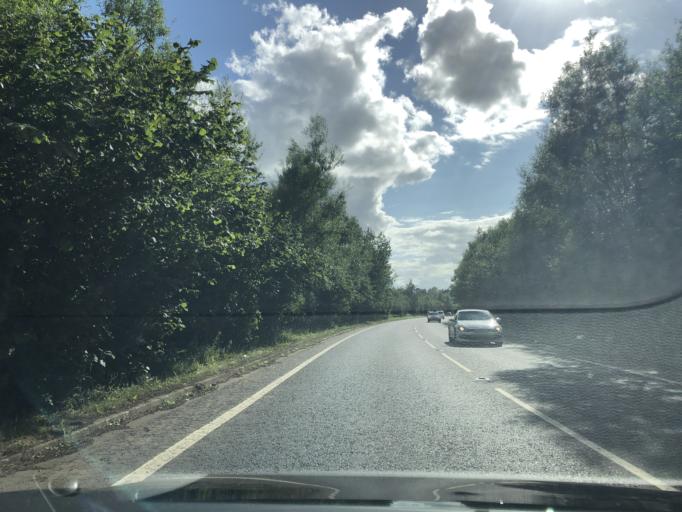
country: GB
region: Northern Ireland
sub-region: Ards District
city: Comber
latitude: 54.5485
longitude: -5.7346
